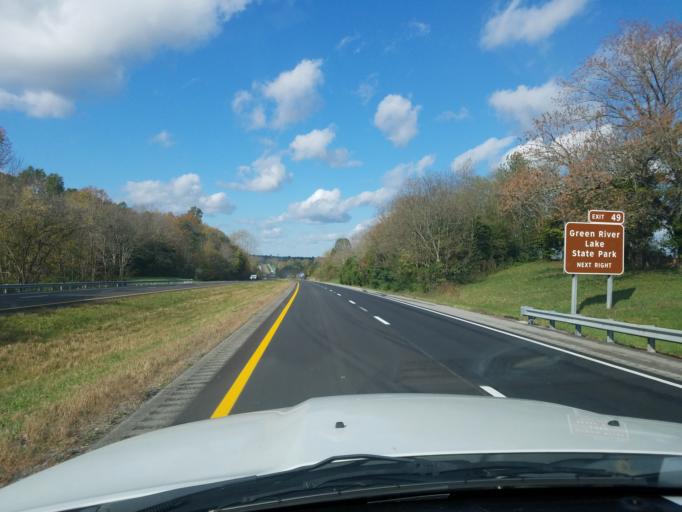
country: US
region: Kentucky
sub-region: Adair County
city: Columbia
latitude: 37.0881
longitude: -85.2702
